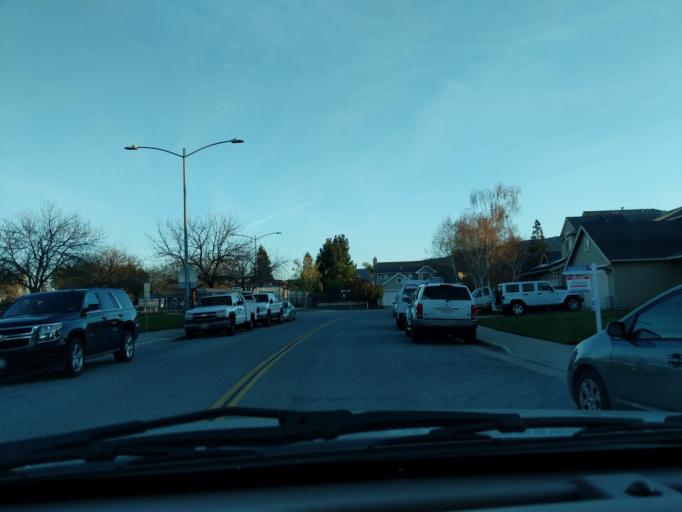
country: US
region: California
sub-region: Santa Clara County
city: Gilroy
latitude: 37.0215
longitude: -121.5955
